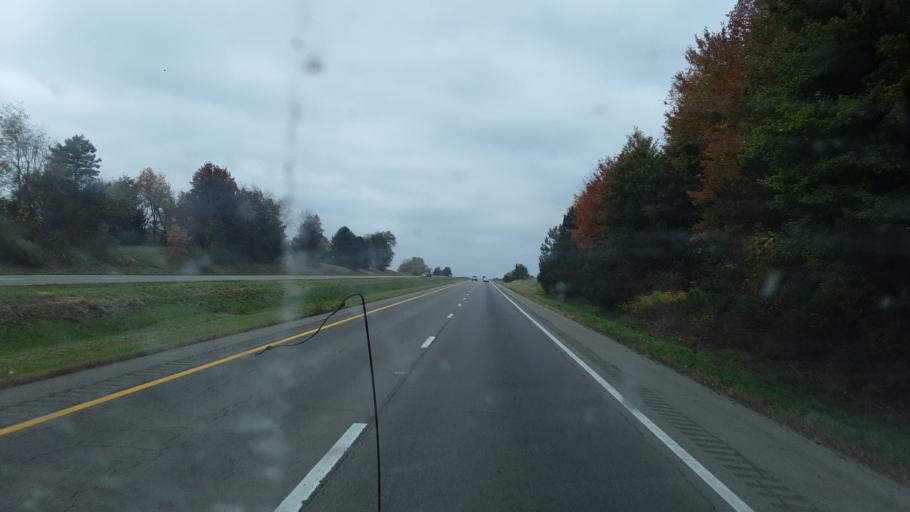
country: US
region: Ohio
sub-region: Wayne County
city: Shreve
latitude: 40.7875
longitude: -82.0806
